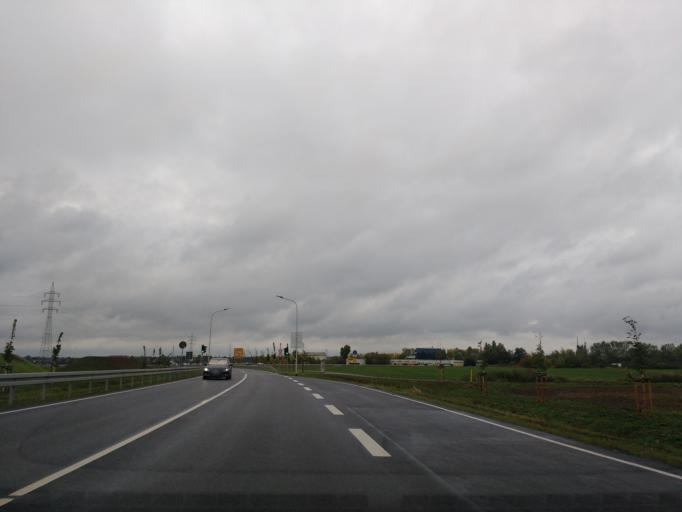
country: DE
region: Saxony-Anhalt
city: Halle (Saale)
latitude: 51.4937
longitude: 12.0158
